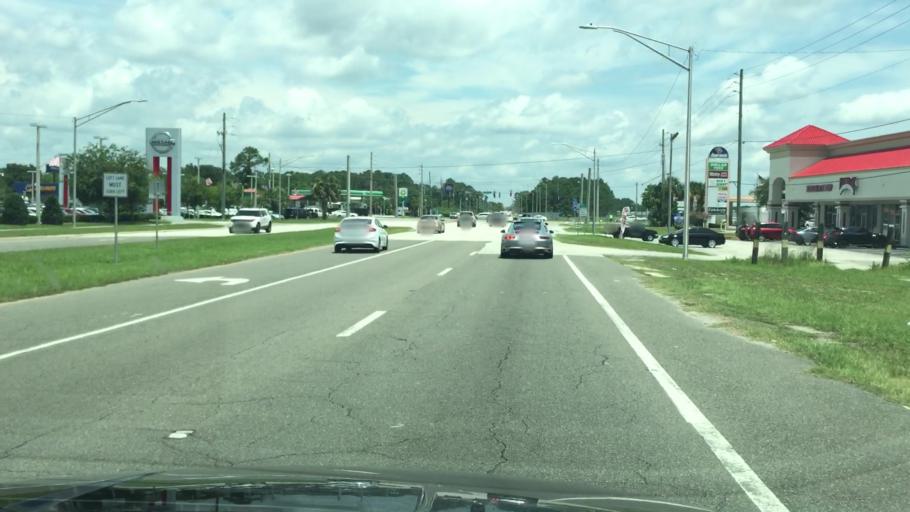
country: US
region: Florida
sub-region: Duval County
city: Atlantic Beach
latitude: 30.3227
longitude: -81.5230
